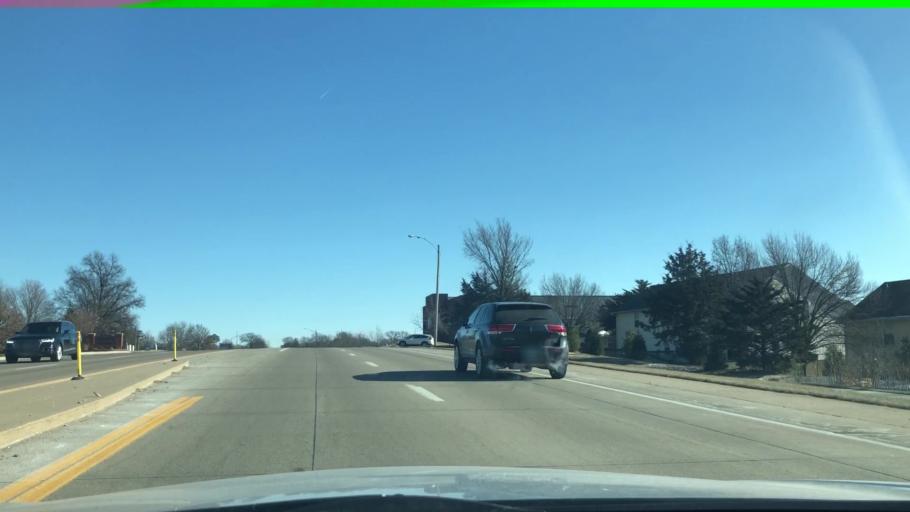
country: US
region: Missouri
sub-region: Boone County
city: Columbia
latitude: 38.9551
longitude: -92.3889
